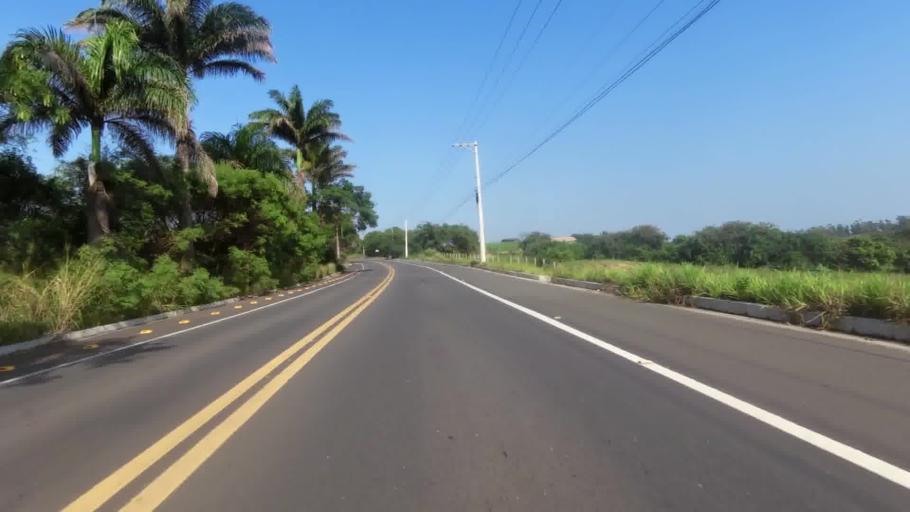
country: BR
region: Espirito Santo
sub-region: Piuma
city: Piuma
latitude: -20.8035
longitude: -40.6059
